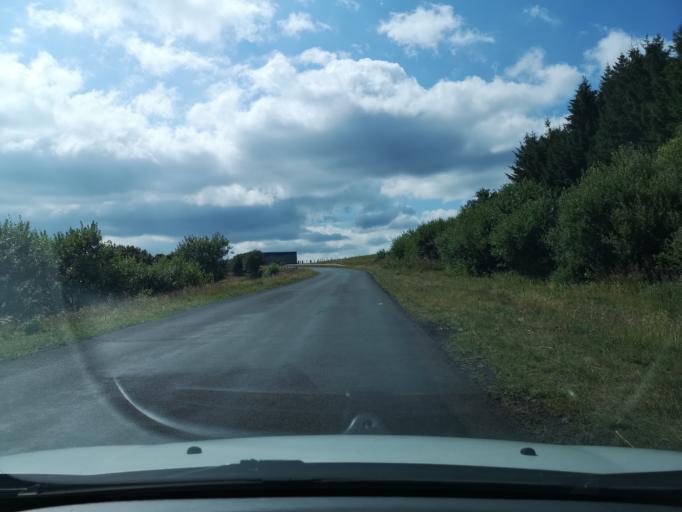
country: FR
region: Auvergne
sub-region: Departement du Puy-de-Dome
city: Mont-Dore
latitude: 45.4985
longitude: 2.8264
